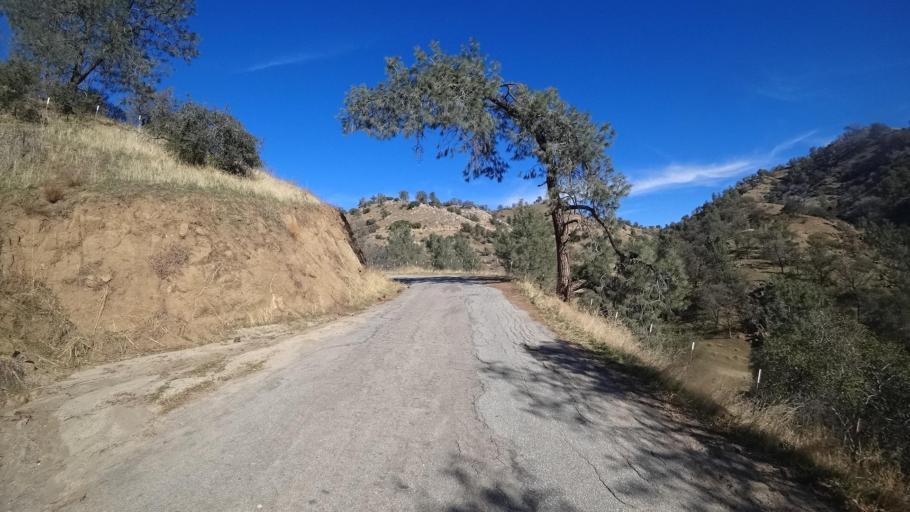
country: US
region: California
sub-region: Kern County
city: Arvin
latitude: 35.4362
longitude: -118.7294
